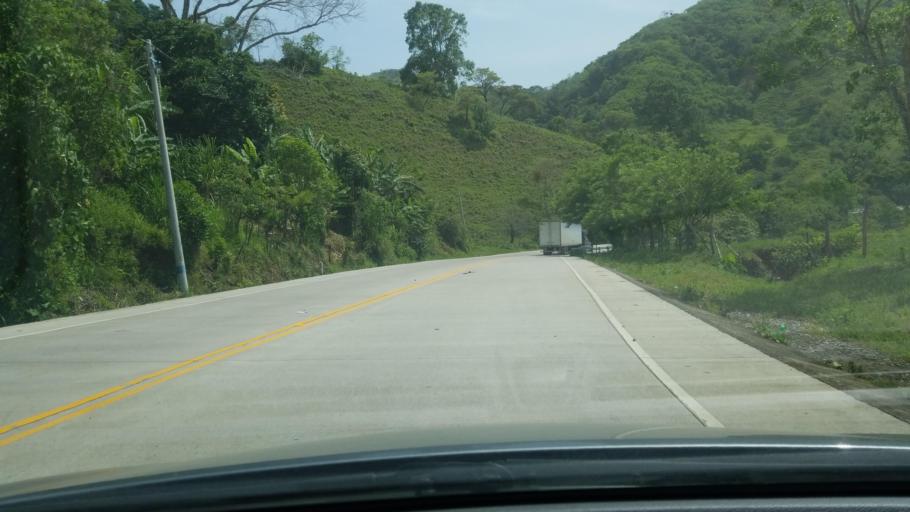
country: HN
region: Copan
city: San Jeronimo
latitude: 14.9558
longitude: -88.9083
